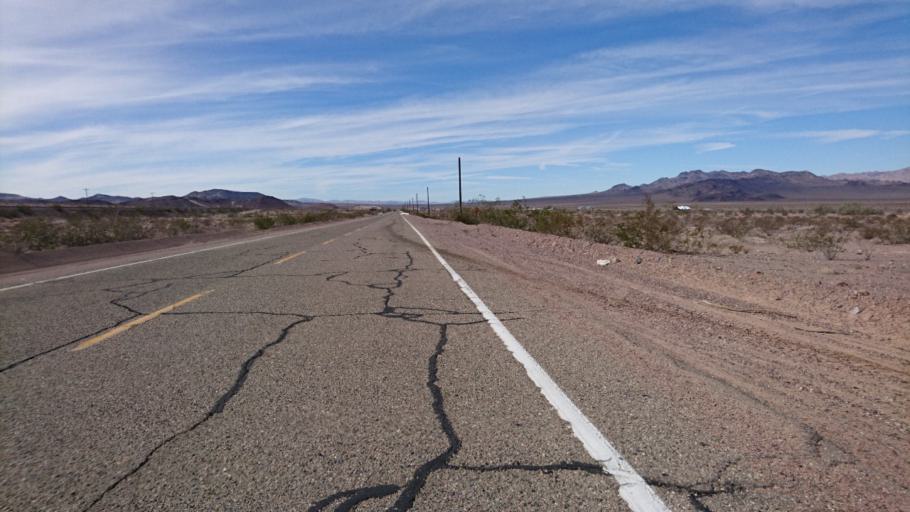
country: US
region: California
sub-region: San Bernardino County
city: Twentynine Palms
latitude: 34.7243
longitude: -116.1465
